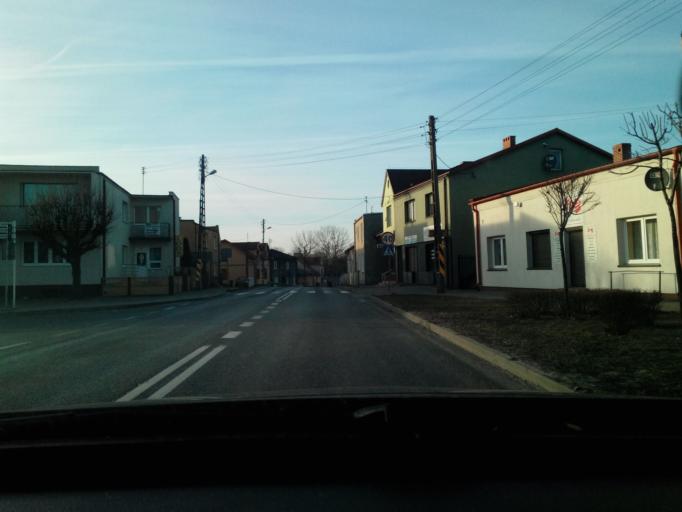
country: PL
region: Kujawsko-Pomorskie
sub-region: Powiat wloclawski
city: Lubien Kujawski
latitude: 52.4055
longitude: 19.1658
